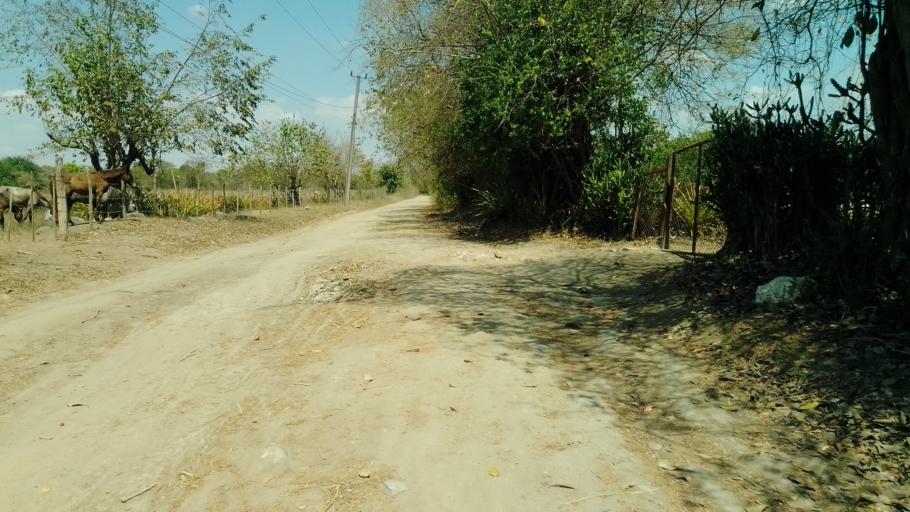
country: CU
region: Las Tunas
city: Las Tunas
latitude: 20.8640
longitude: -76.9883
